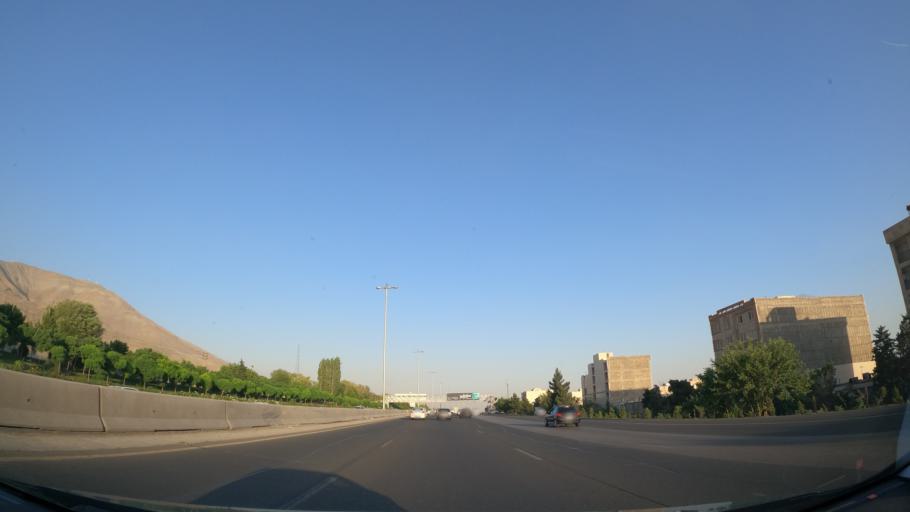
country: IR
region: Alborz
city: Karaj
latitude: 35.7840
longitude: 51.0291
